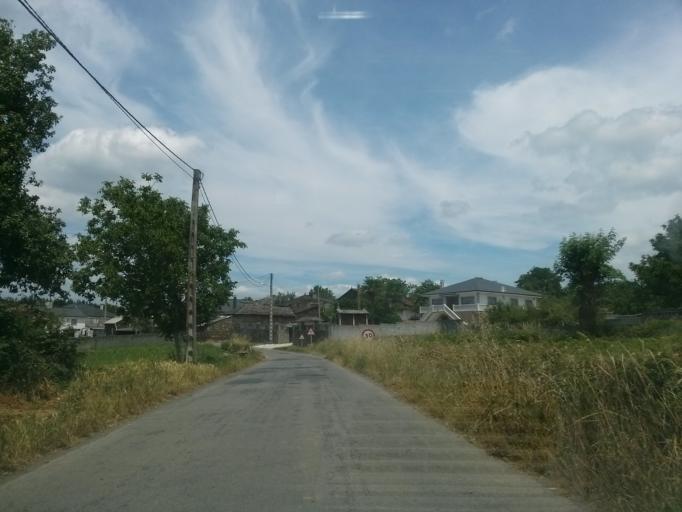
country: ES
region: Galicia
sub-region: Provincia de Lugo
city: Lugo
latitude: 43.0389
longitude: -7.6083
